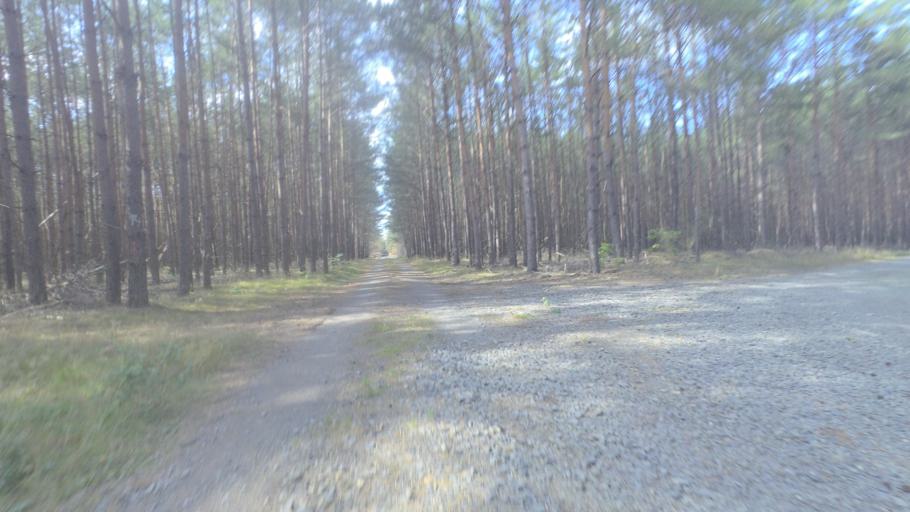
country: DE
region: Brandenburg
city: Munchehofe
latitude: 52.1770
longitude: 13.8724
